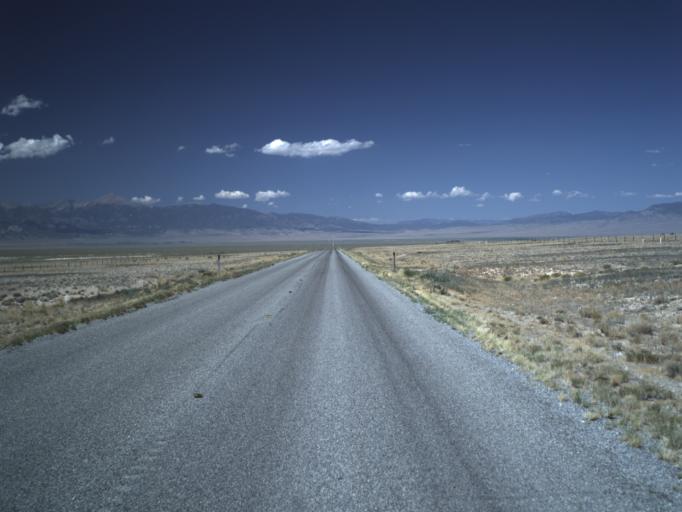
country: US
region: Nevada
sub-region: White Pine County
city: McGill
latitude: 39.0403
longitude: -113.8299
